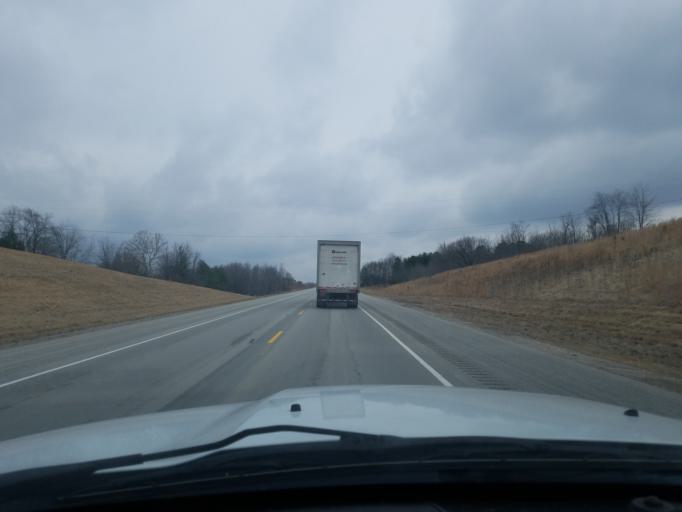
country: US
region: Indiana
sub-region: Perry County
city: Tell City
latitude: 38.1182
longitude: -86.6077
